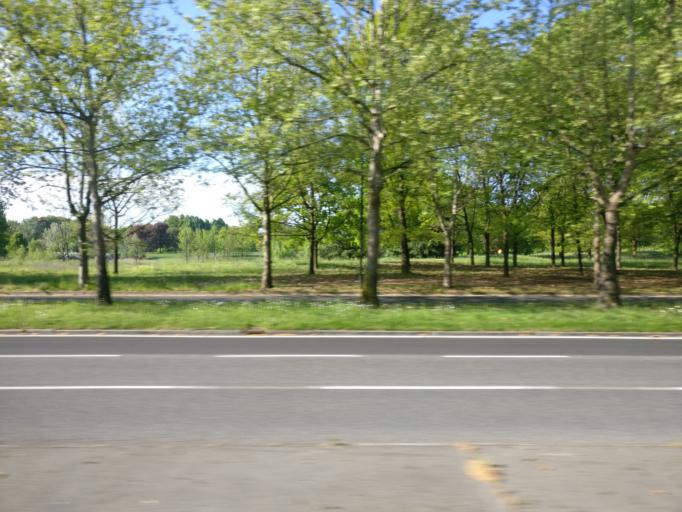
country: IT
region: Piedmont
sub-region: Provincia di Torino
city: Savonera
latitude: 45.0926
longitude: 7.6357
